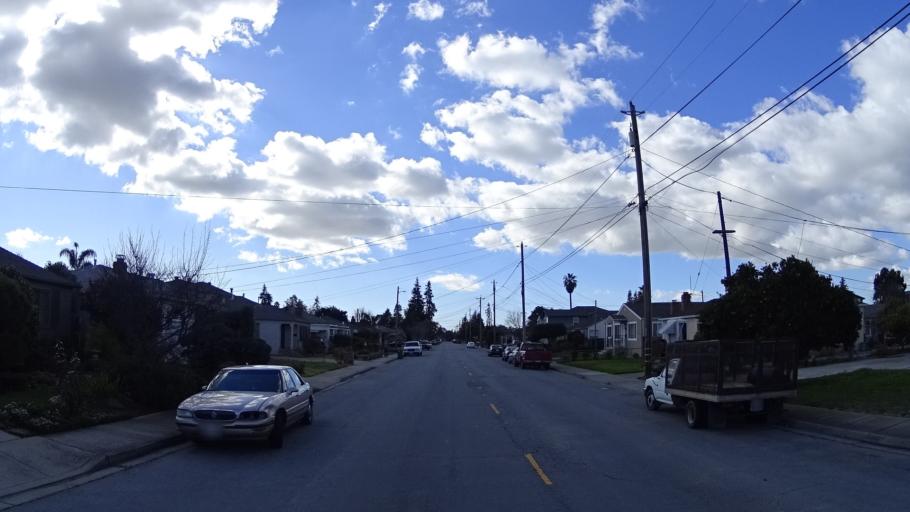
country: US
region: California
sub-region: Alameda County
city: Cherryland
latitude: 37.6797
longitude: -122.1060
